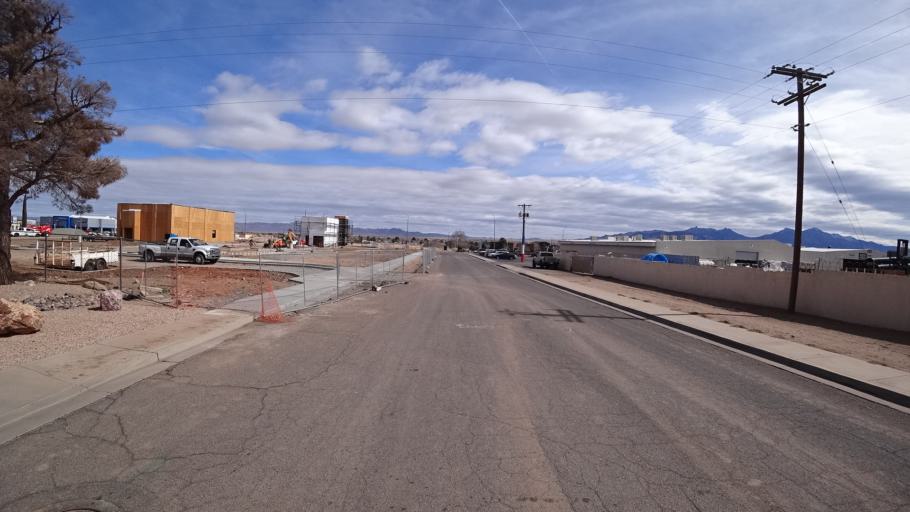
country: US
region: Arizona
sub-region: Mohave County
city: New Kingman-Butler
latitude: 35.2296
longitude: -114.0381
